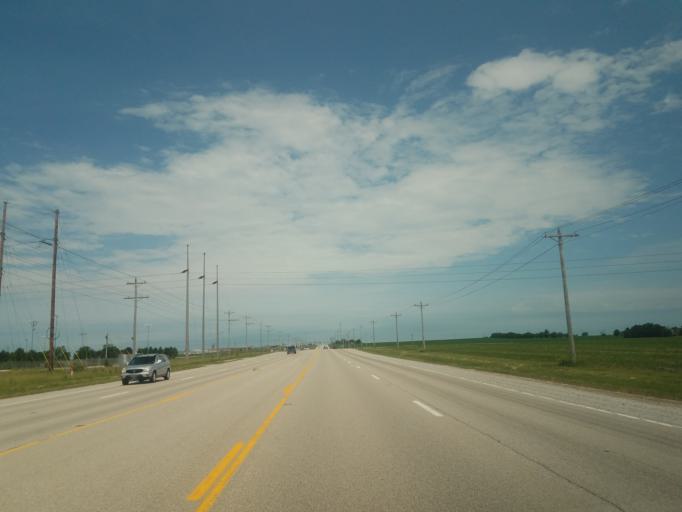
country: US
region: Illinois
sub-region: McLean County
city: Downs
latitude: 40.4541
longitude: -88.9018
